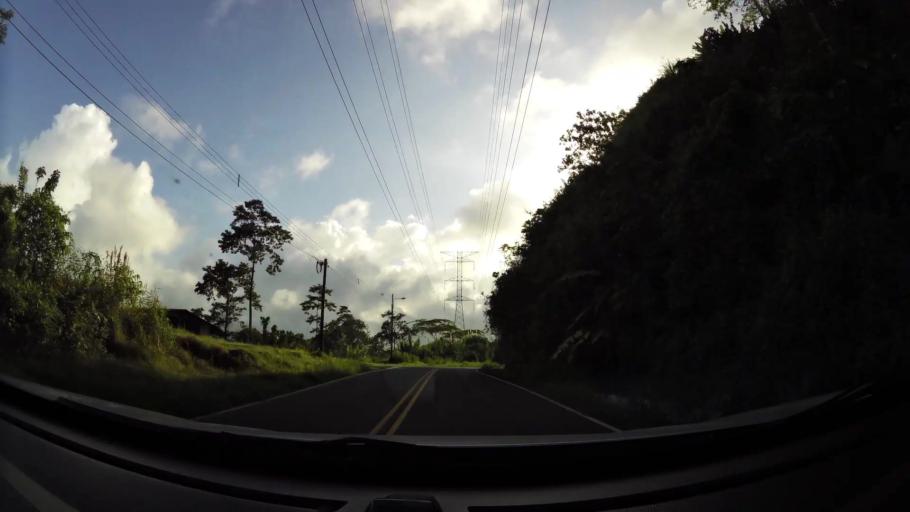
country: CR
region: Limon
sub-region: Canton de Siquirres
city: Siquirres
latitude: 10.0261
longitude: -83.5566
